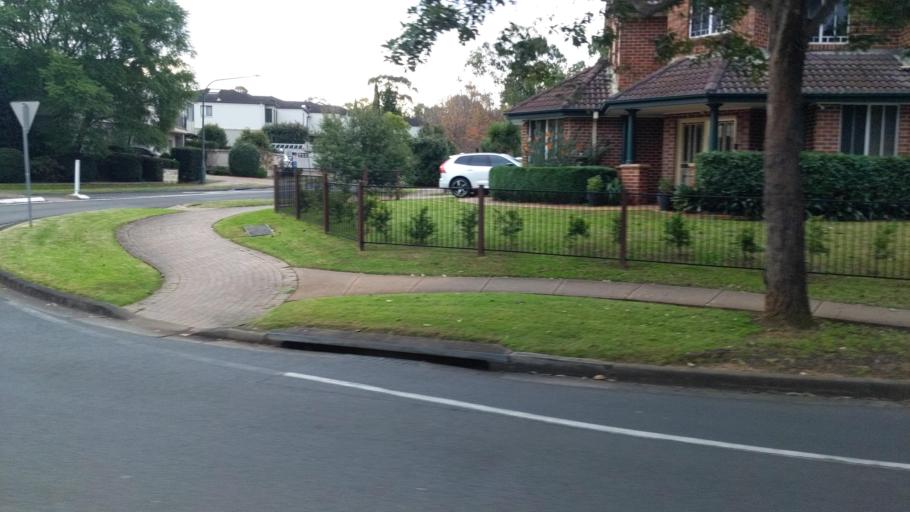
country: AU
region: New South Wales
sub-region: The Hills Shire
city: Baulkham Hills
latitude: -33.7451
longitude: 150.9604
